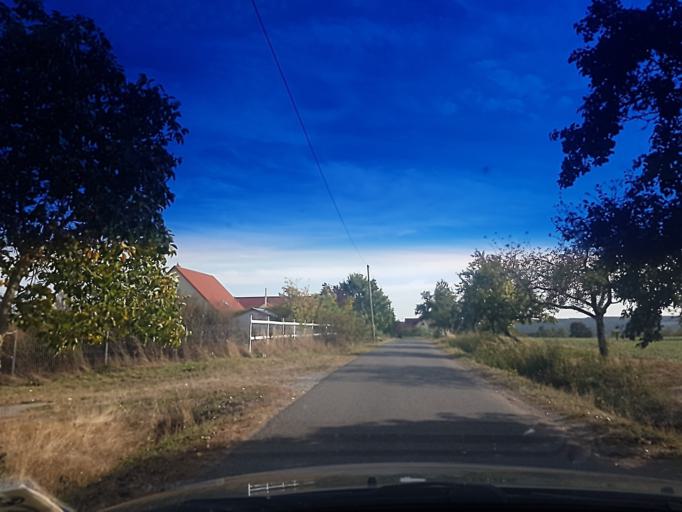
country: DE
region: Bavaria
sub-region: Upper Franconia
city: Burgwindheim
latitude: 49.7786
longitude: 10.5441
